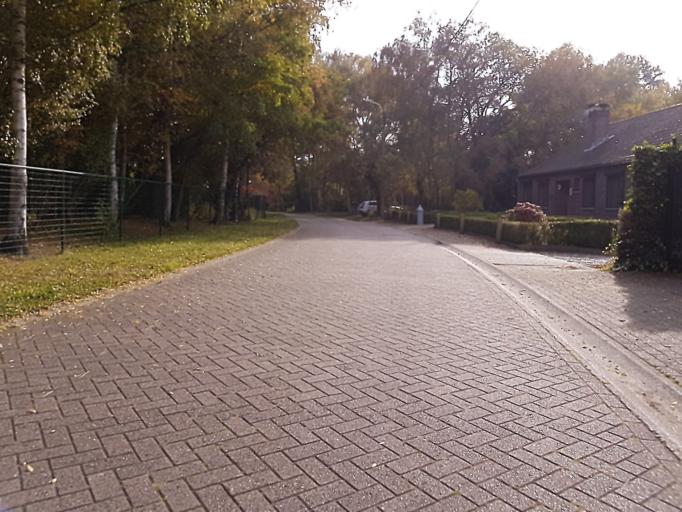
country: BE
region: Flanders
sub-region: Provincie Antwerpen
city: Sint-Katelijne-Waver
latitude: 51.0582
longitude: 4.5104
